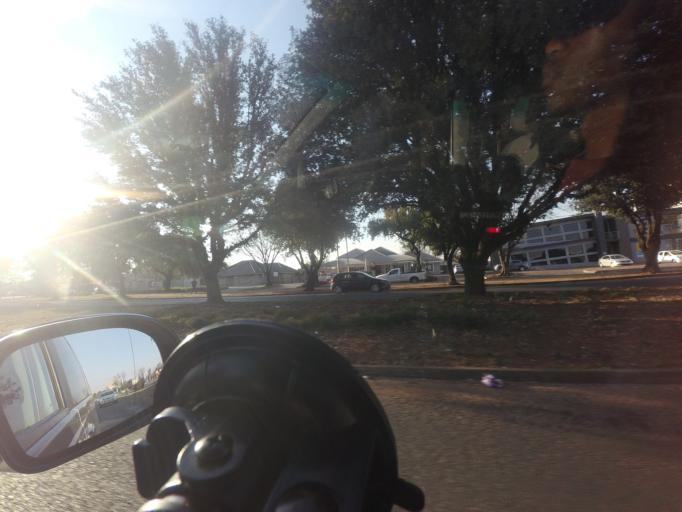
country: ZA
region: Gauteng
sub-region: Sedibeng District Municipality
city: Vereeniging
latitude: -26.6591
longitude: 27.9687
